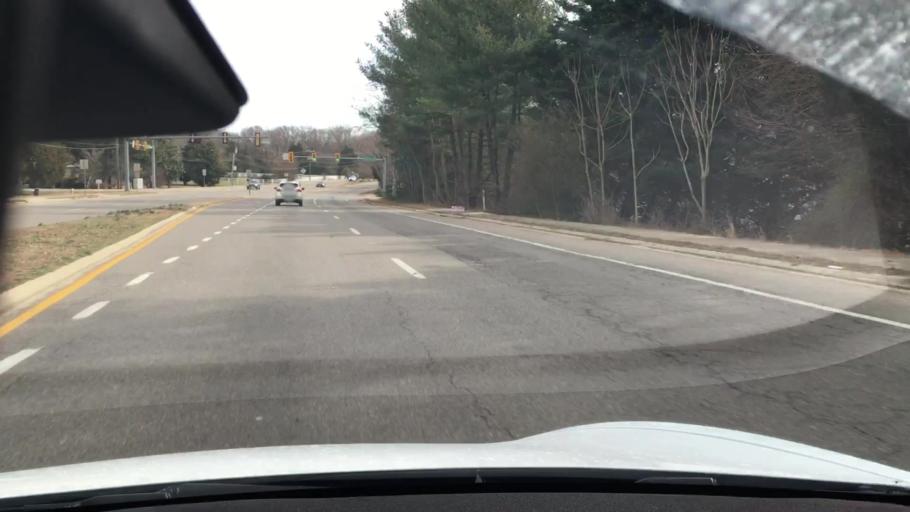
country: US
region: Virginia
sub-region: Chesterfield County
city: Bon Air
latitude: 37.5281
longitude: -77.6264
